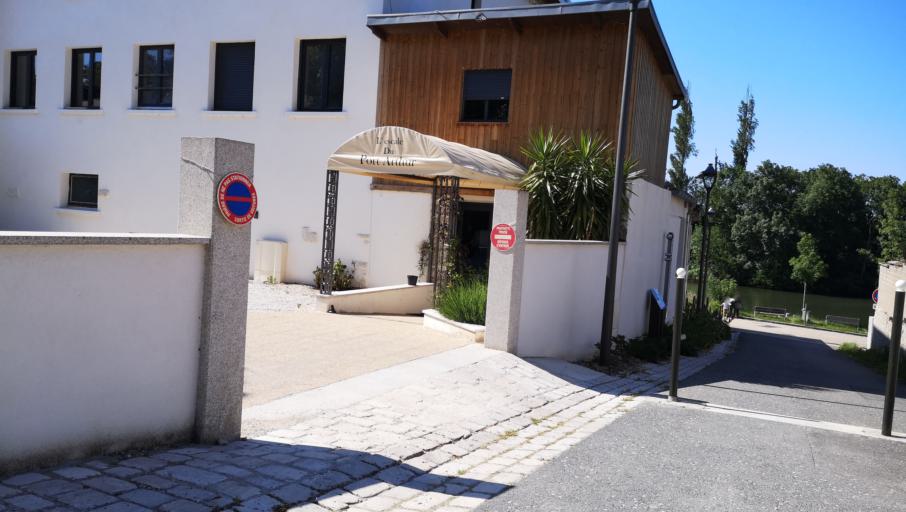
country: FR
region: Centre
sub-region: Departement du Loiret
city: Saint-Hilaire-Saint-Mesmin
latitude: 47.8666
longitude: 1.8272
